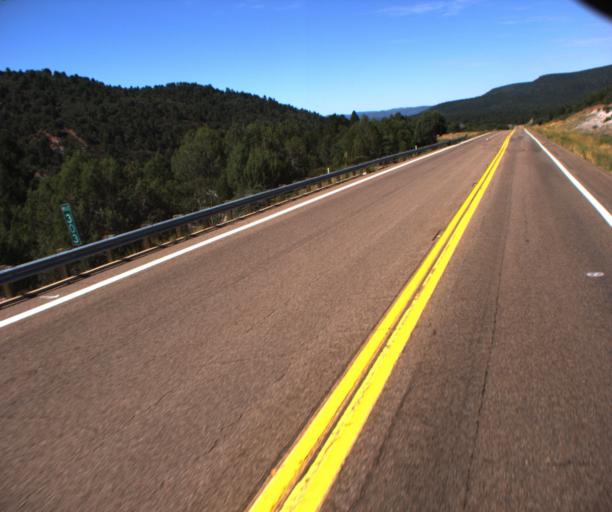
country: US
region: Arizona
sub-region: Navajo County
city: Cibecue
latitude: 33.8715
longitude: -110.4023
